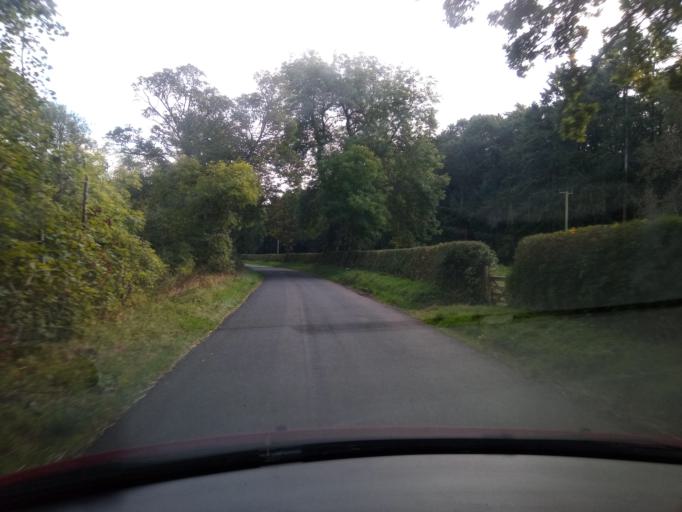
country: GB
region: Scotland
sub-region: The Scottish Borders
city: Kelso
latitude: 55.5065
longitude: -2.3514
